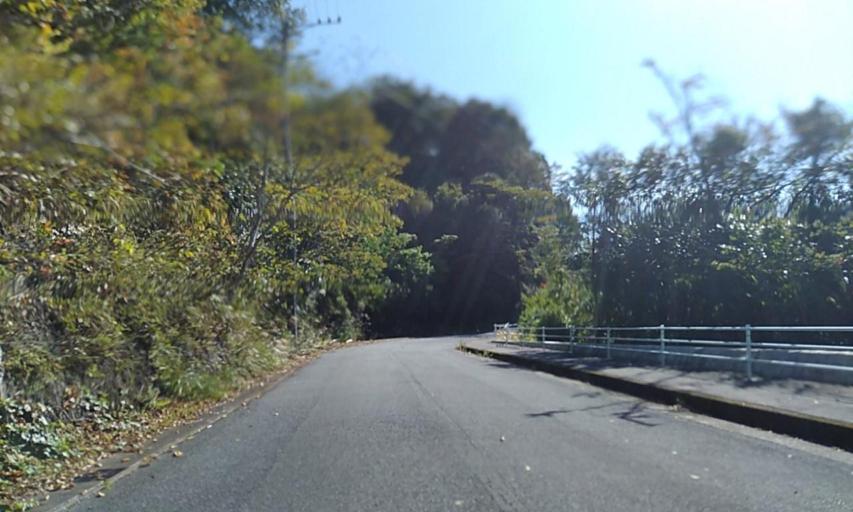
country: JP
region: Mie
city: Owase
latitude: 34.1636
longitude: 136.2835
